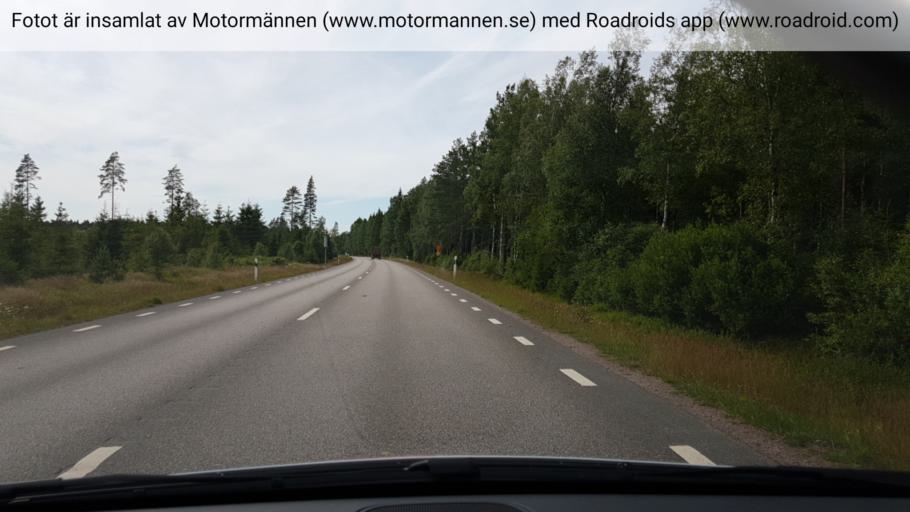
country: SE
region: Vaestra Goetaland
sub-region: Hjo Kommun
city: Hjo
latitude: 58.3400
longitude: 14.2269
